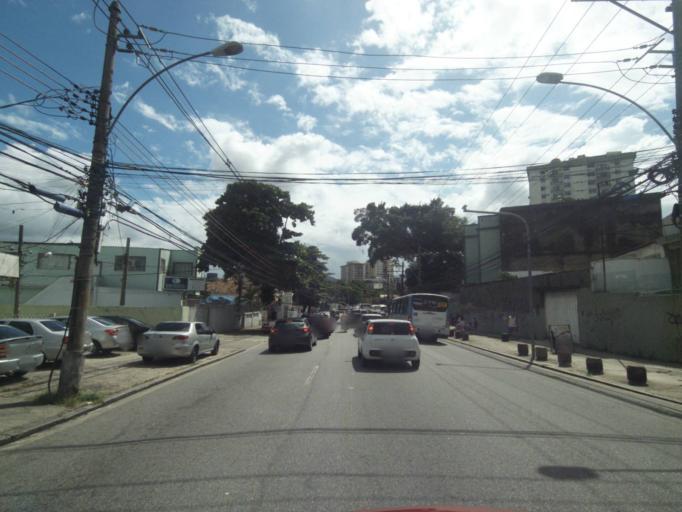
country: BR
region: Rio de Janeiro
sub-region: Sao Joao De Meriti
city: Sao Joao de Meriti
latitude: -22.9258
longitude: -43.3571
